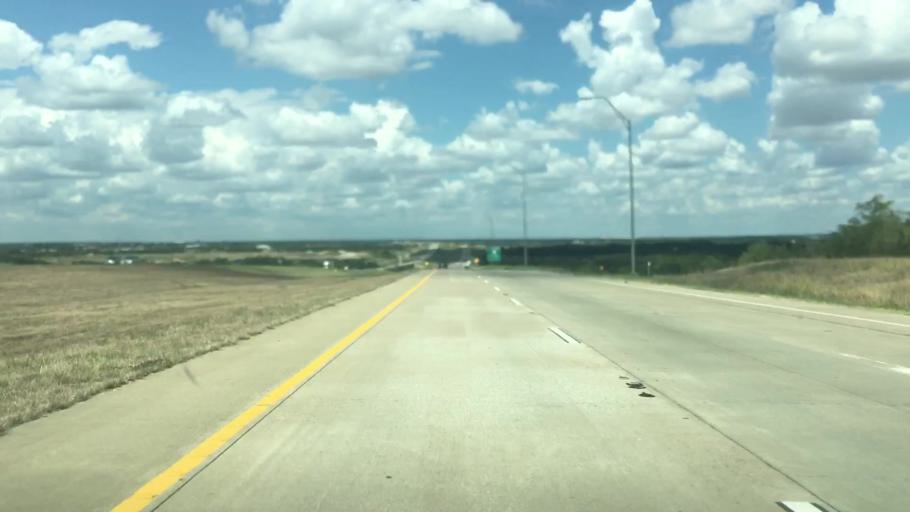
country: US
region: Texas
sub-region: Williamson County
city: Georgetown
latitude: 30.6485
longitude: -97.6329
